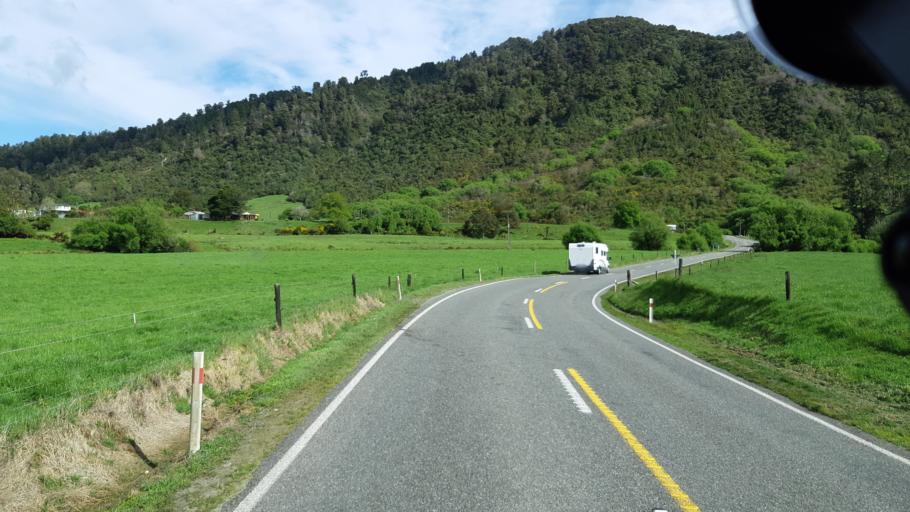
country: NZ
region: West Coast
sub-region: Buller District
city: Westport
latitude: -41.8605
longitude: 171.9404
